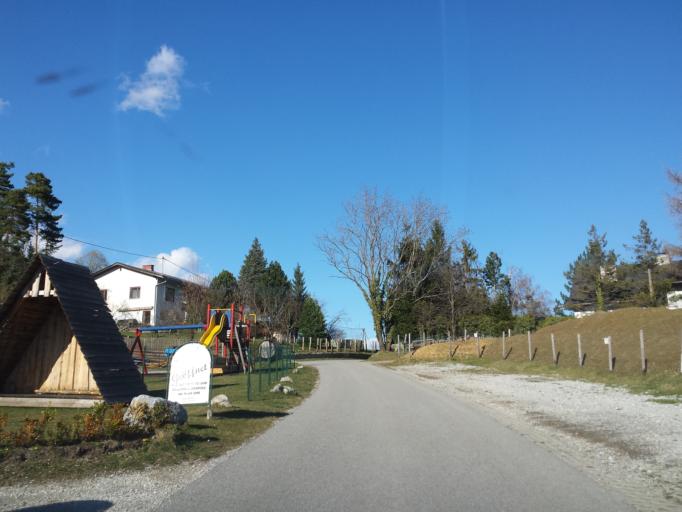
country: AT
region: Styria
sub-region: Politischer Bezirk Graz-Umgebung
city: Sankt Radegund bei Graz
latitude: 47.1683
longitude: 15.4785
